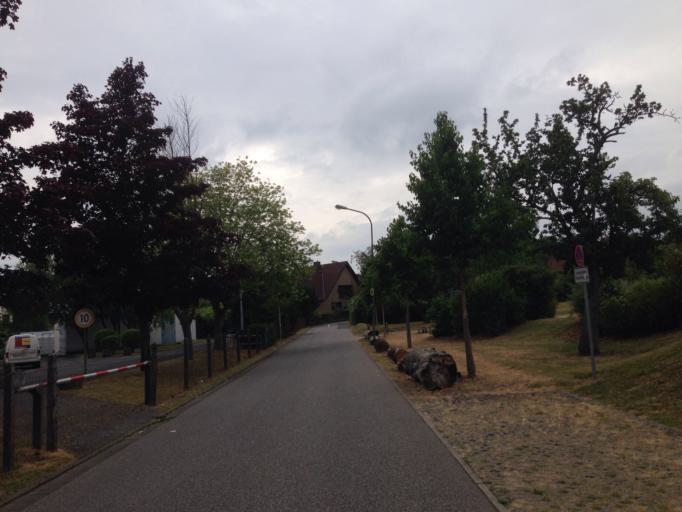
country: DE
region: Hesse
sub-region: Regierungsbezirk Giessen
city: Giessen
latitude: 50.5773
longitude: 8.6913
